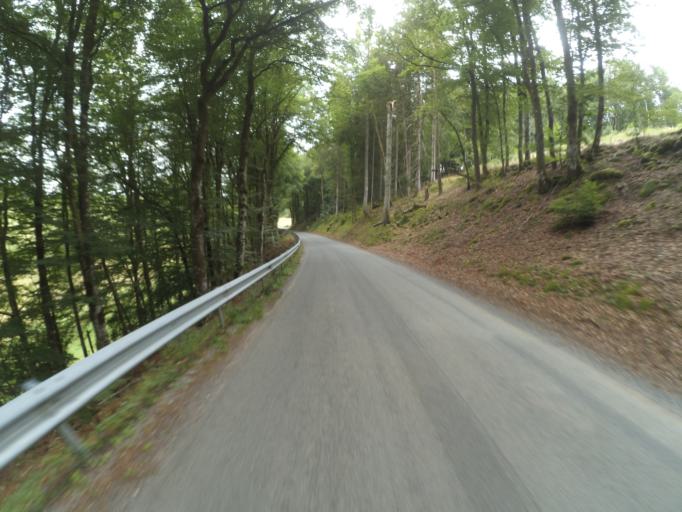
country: FR
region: Limousin
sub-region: Departement de la Correze
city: Meymac
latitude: 45.6557
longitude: 2.1070
